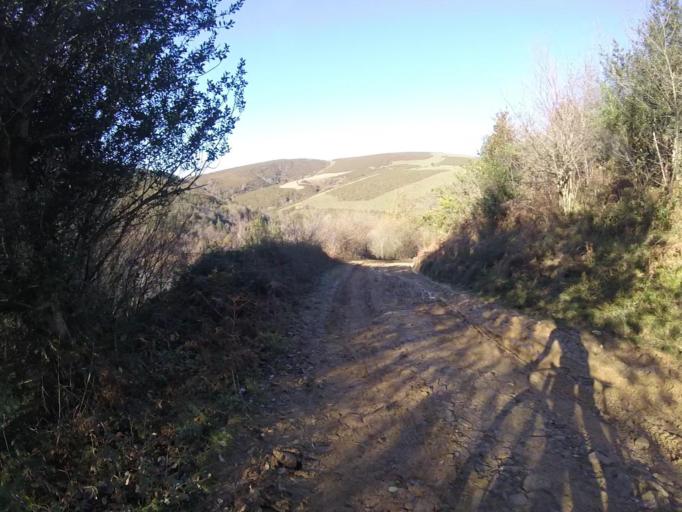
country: ES
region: Navarre
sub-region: Provincia de Navarra
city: Bera
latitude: 43.3174
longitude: -1.7117
